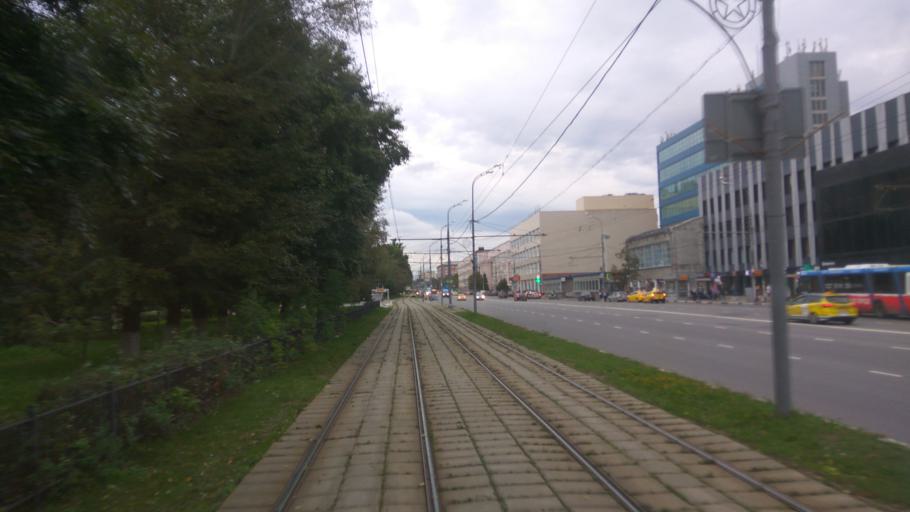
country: RU
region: Moscow
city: Taganskiy
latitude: 55.7167
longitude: 37.6774
